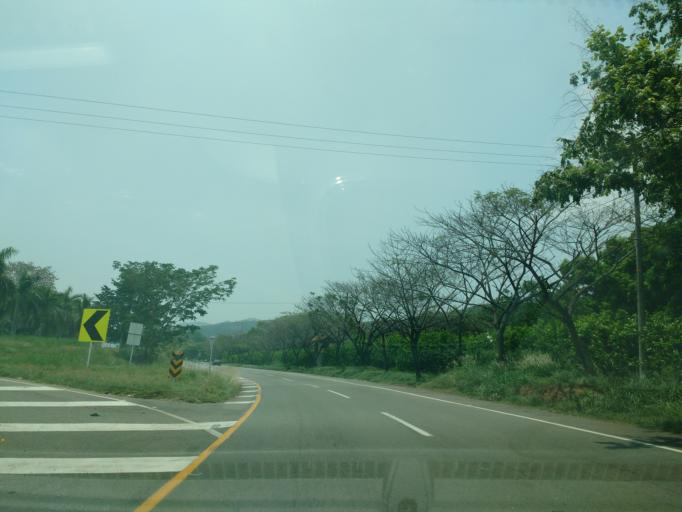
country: CO
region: Tolima
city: Melgar
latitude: 4.2300
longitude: -74.7034
